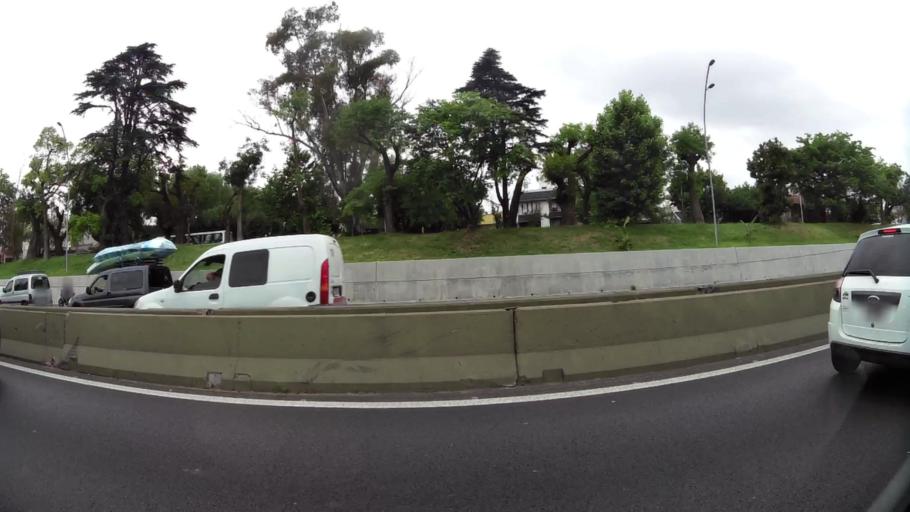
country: AR
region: Buenos Aires
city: Caseros
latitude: -34.6140
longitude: -58.5302
